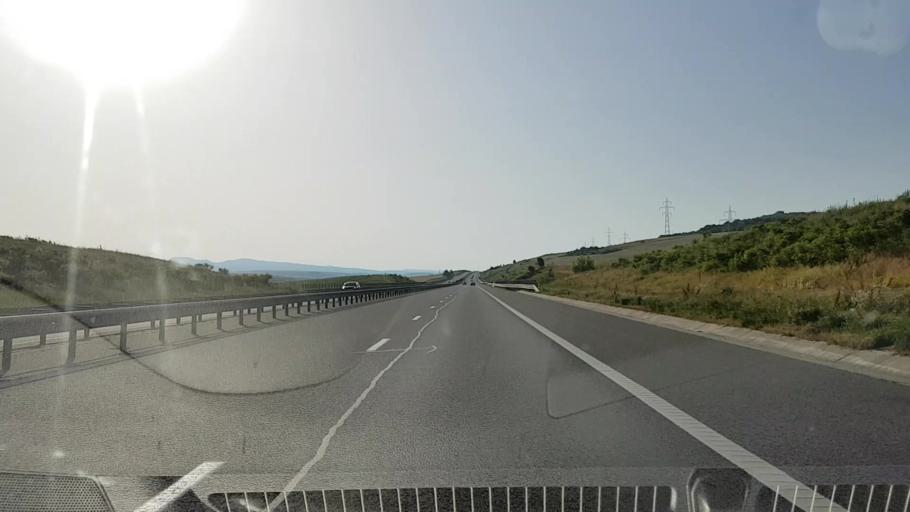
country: RO
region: Cluj
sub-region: Comuna Petrestii De Jos
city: Petrestii de Jos
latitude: 46.6039
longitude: 23.6156
